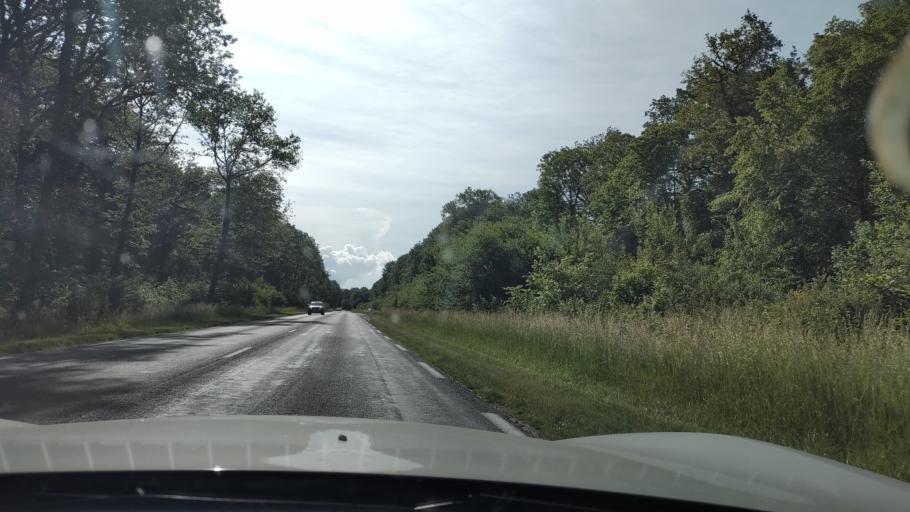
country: FR
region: Ile-de-France
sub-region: Departement de Seine-et-Marne
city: Sourdun
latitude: 48.5296
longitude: 3.3952
